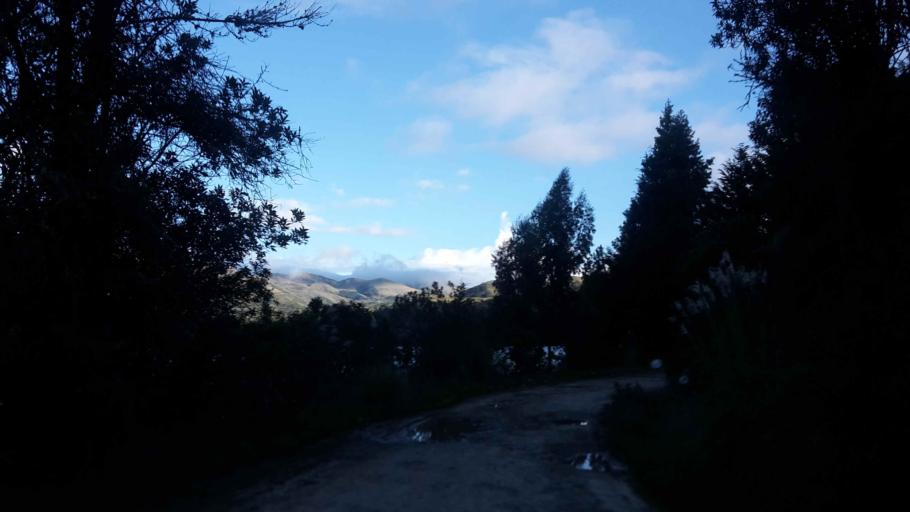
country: BO
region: Cochabamba
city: Colomi
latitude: -17.2543
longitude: -65.9042
